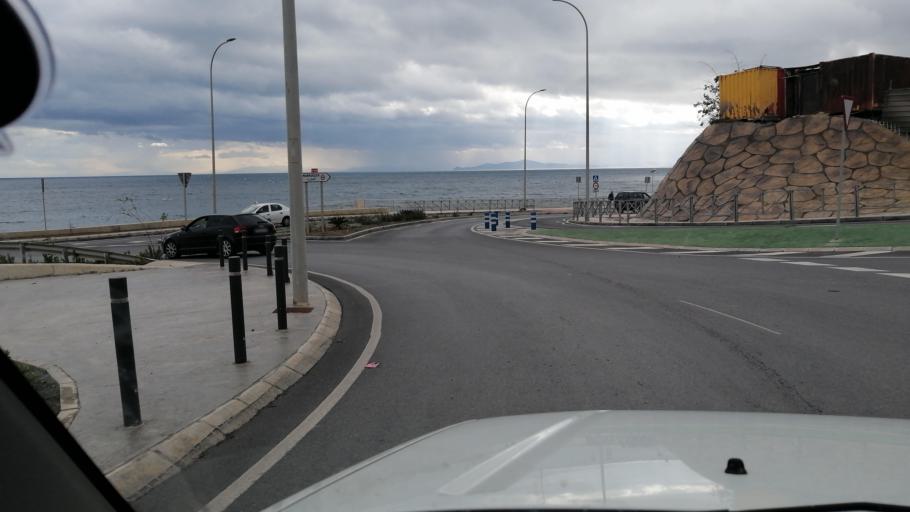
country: ES
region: Ceuta
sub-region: Ceuta
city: Ceuta
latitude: 35.8766
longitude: -5.3412
